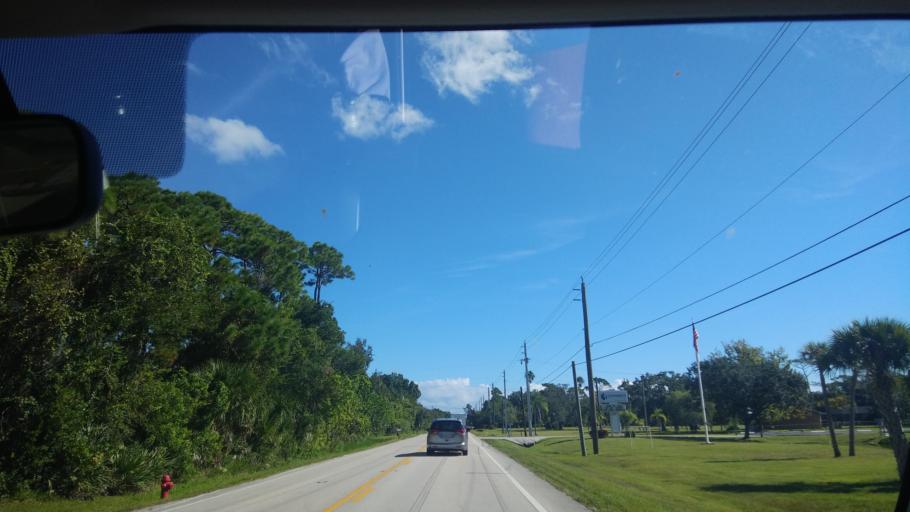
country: US
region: Florida
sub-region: Indian River County
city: Roseland
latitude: 27.8268
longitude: -80.5027
